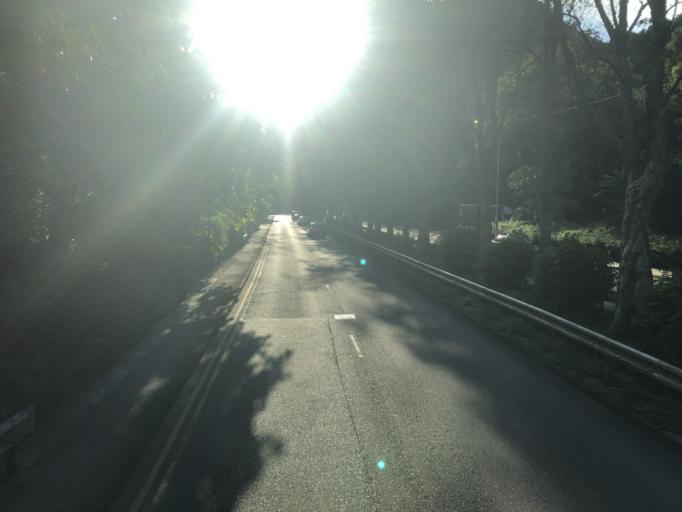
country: HK
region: Wong Tai Sin
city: Wong Tai Sin
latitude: 22.3340
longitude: 114.2324
